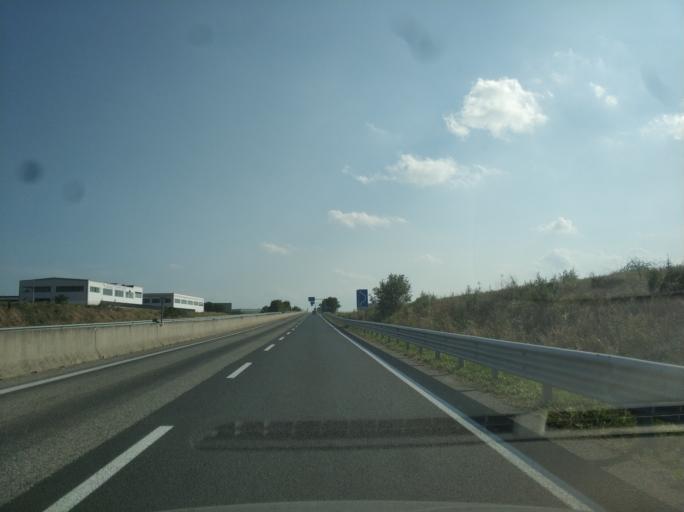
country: IT
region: Piedmont
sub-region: Provincia di Cuneo
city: Roreto
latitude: 44.6744
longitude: 7.8274
